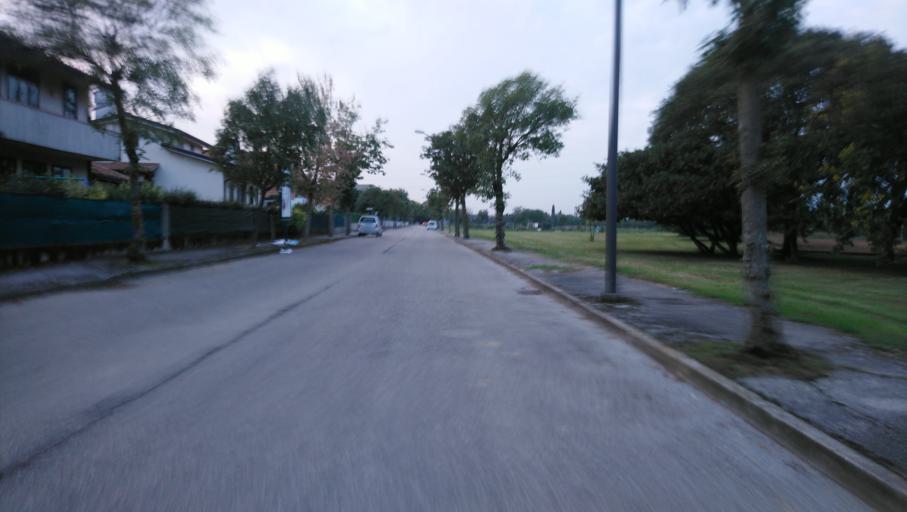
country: IT
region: Veneto
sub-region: Provincia di Treviso
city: Treviso
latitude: 45.6949
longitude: 12.2325
